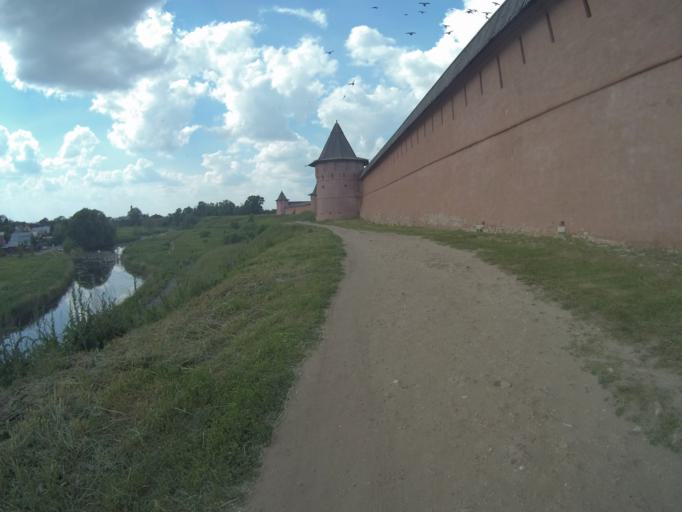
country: RU
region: Vladimir
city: Suzdal'
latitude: 56.4319
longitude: 40.4397
